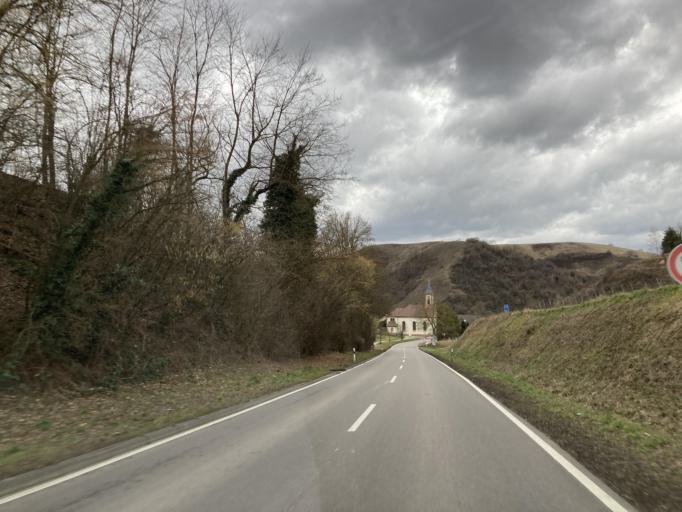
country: DE
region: Baden-Wuerttemberg
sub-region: Freiburg Region
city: Botzingen
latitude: 48.0902
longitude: 7.6872
